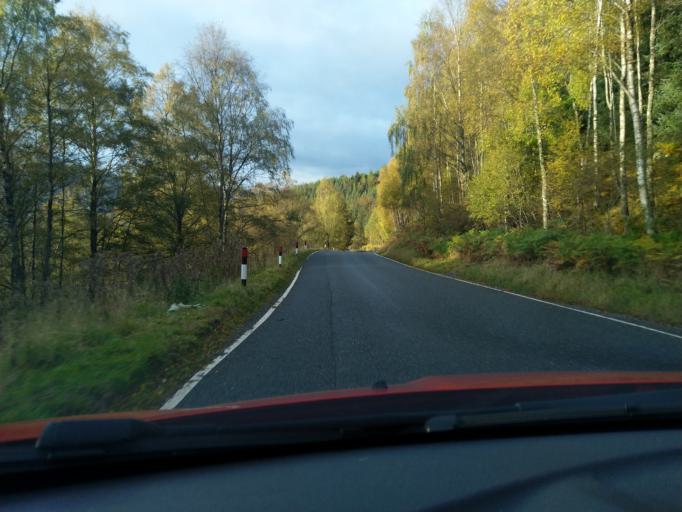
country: GB
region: Scotland
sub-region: Perth and Kinross
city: Aberfeldy
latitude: 56.7174
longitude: -4.1190
